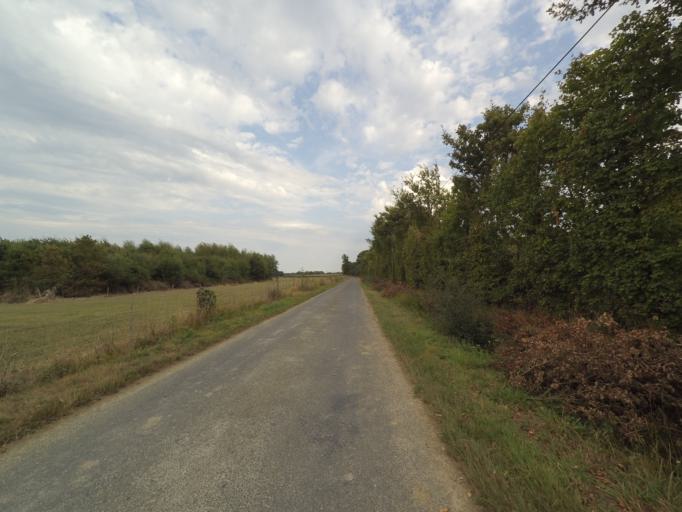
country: FR
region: Pays de la Loire
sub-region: Departement de la Vendee
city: Bouffere
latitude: 46.9815
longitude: -1.3725
